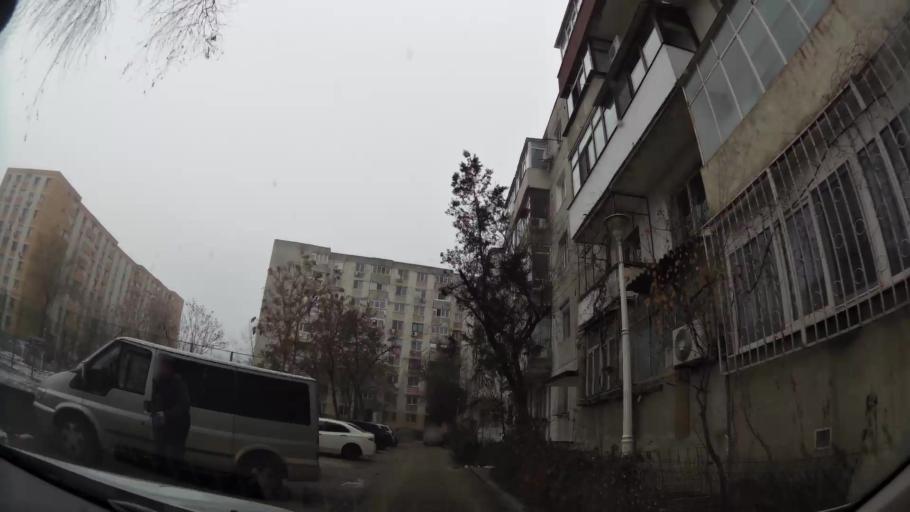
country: RO
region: Ilfov
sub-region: Comuna Chiajna
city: Rosu
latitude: 44.4544
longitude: 26.0405
